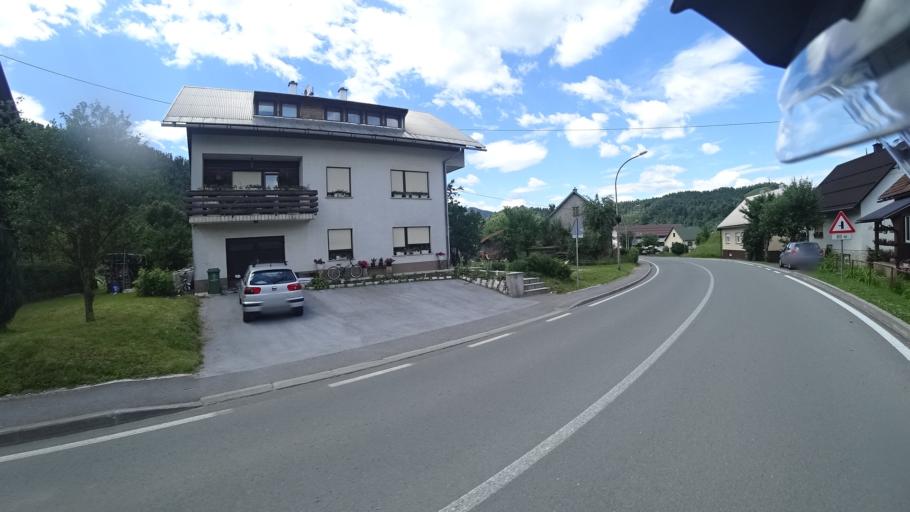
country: SI
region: Osilnica
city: Osilnica
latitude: 45.5113
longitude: 14.6360
